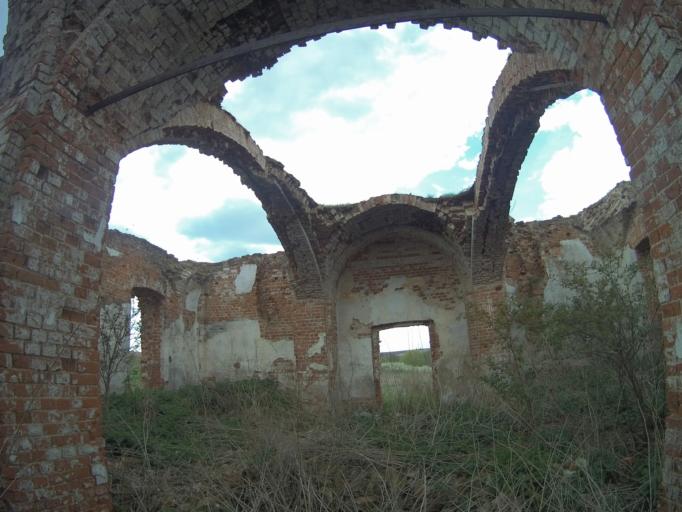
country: RU
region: Vladimir
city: Vladimir
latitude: 56.2961
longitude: 40.2613
